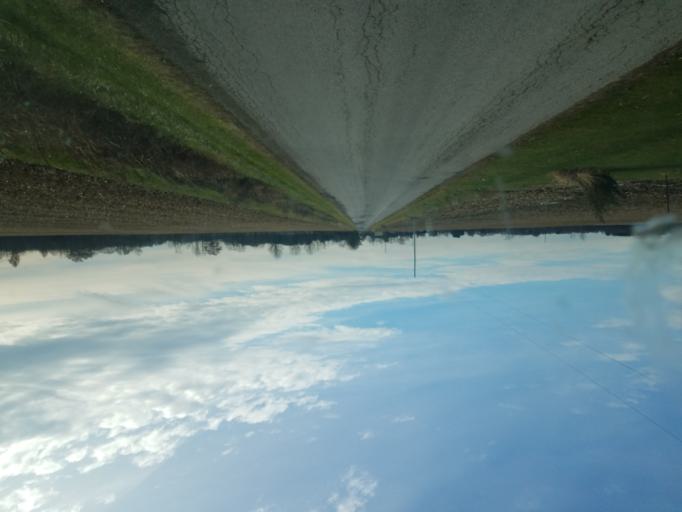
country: US
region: Ohio
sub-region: Crawford County
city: Galion
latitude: 40.6983
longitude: -82.8535
